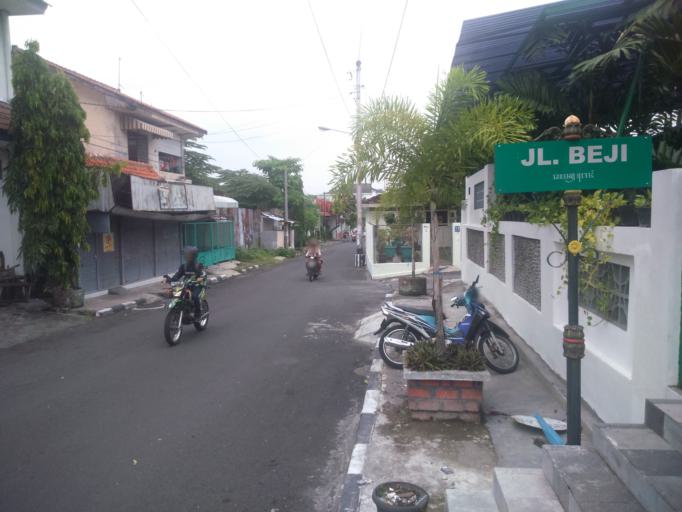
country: ID
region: Daerah Istimewa Yogyakarta
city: Yogyakarta
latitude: -7.8008
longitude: 110.3731
